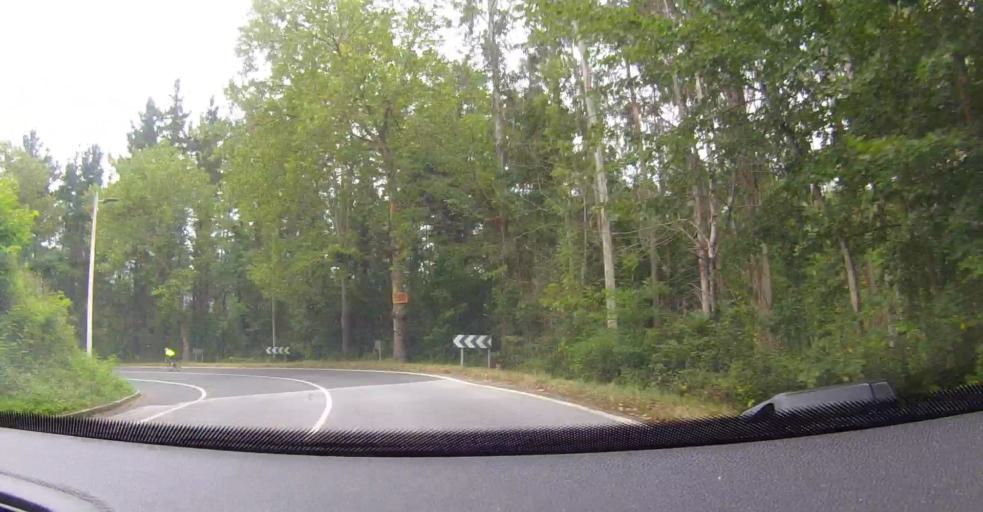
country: ES
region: Basque Country
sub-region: Bizkaia
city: Balmaseda
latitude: 43.2447
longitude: -3.2545
